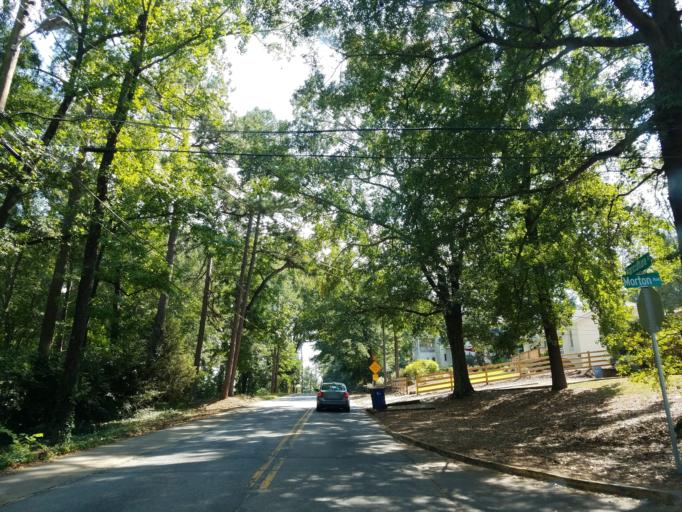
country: US
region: Georgia
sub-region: Clarke County
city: Athens
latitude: 33.9387
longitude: -83.3763
